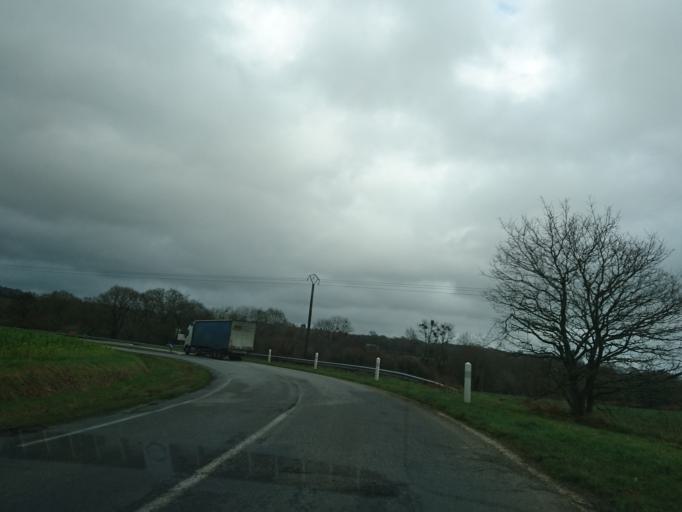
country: FR
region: Brittany
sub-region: Departement des Cotes-d'Armor
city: Rostrenen
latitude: 48.2132
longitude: -3.3239
